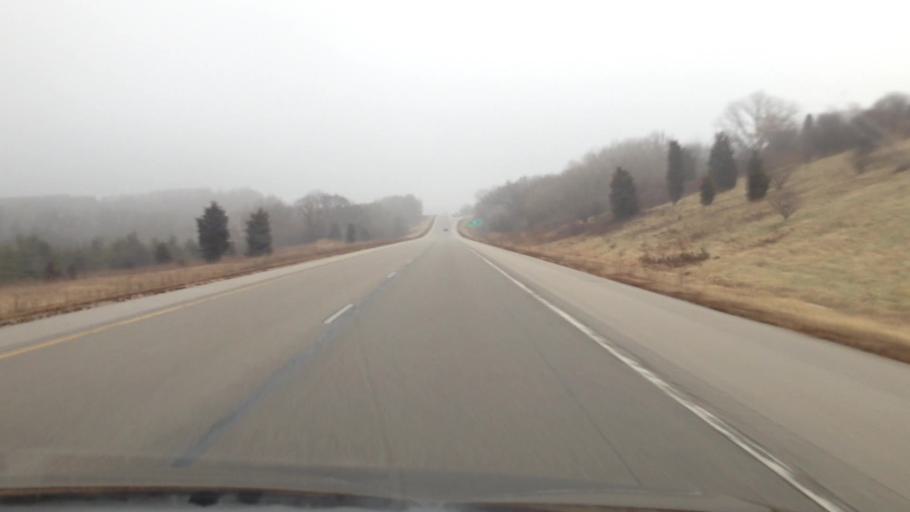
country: US
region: Wisconsin
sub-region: Walworth County
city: East Troy
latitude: 42.7691
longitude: -88.4191
